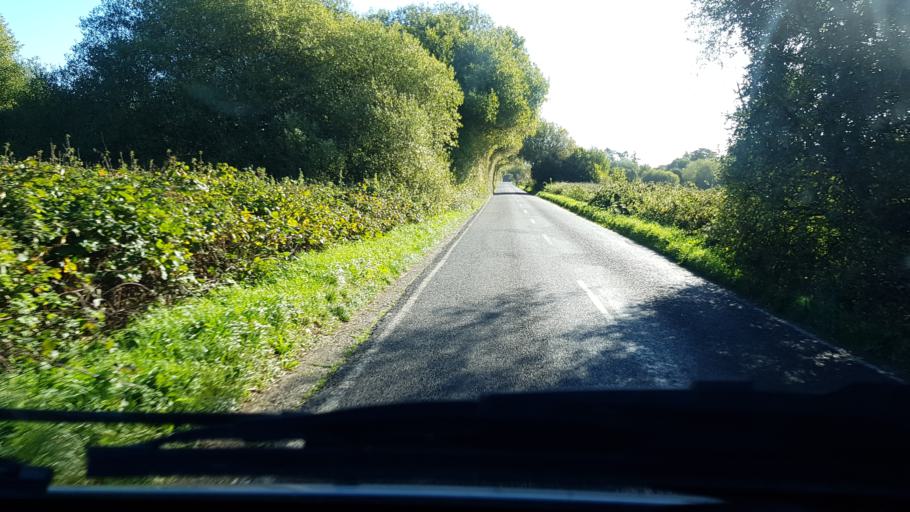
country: GB
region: England
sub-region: Surrey
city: Cranleigh
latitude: 51.1618
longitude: -0.4997
